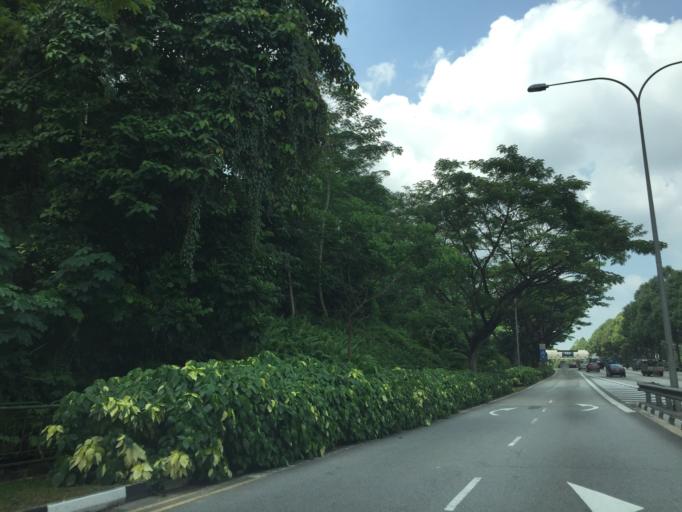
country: SG
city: Singapore
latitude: 1.3319
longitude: 103.8178
